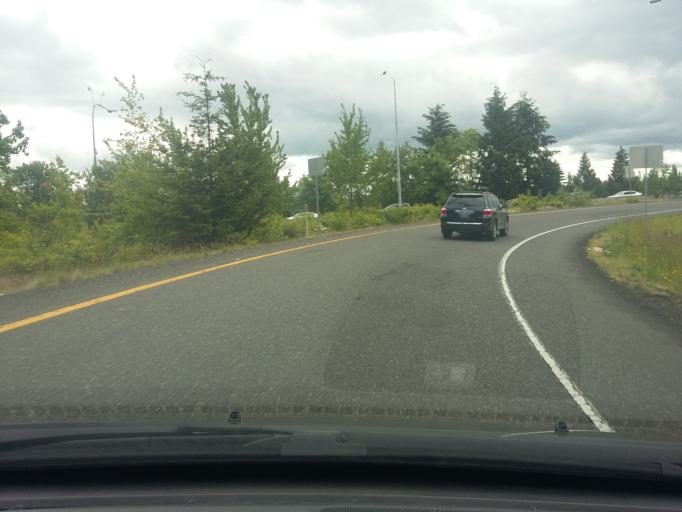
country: US
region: Washington
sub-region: Clark County
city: Barberton
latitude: 45.6841
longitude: -122.5923
